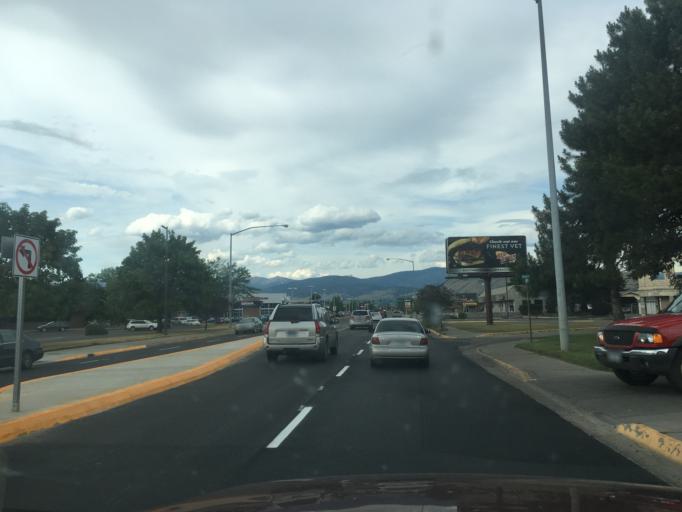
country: US
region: Montana
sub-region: Missoula County
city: Orchard Homes
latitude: 46.8442
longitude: -114.0247
